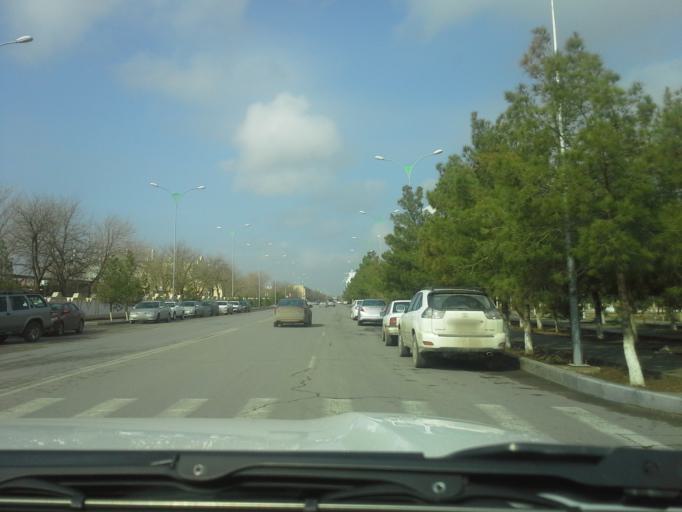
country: TM
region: Mary
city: Mary
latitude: 37.5910
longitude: 61.8390
